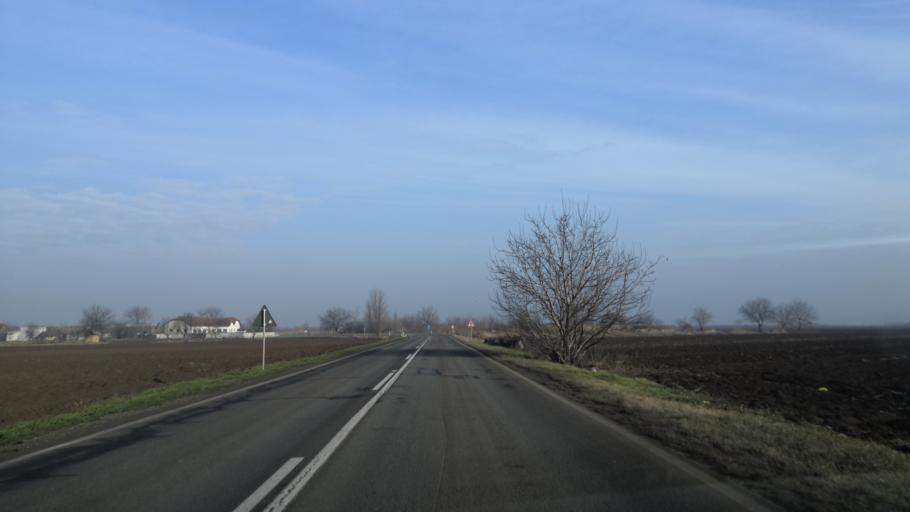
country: RS
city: Kisac
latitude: 45.3406
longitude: 19.7336
